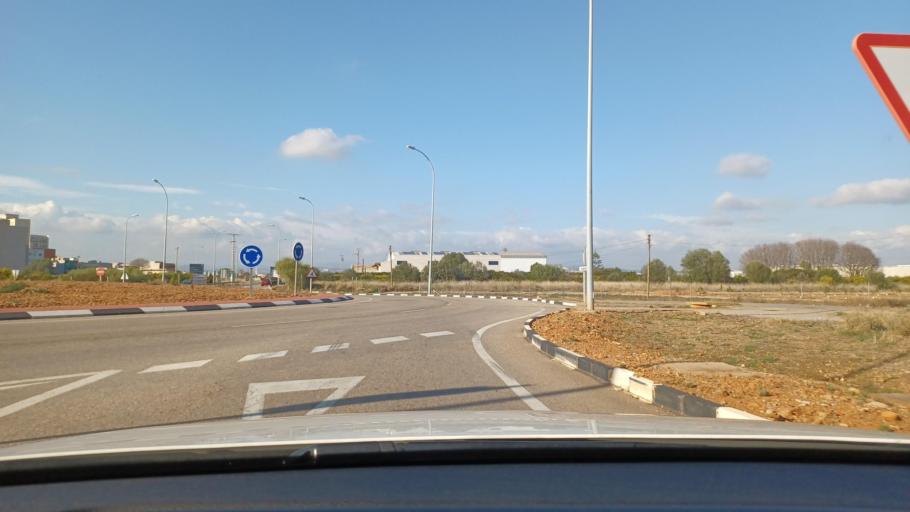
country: ES
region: Valencia
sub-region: Provincia de Castello
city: Betxi
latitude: 39.9270
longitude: -0.1915
